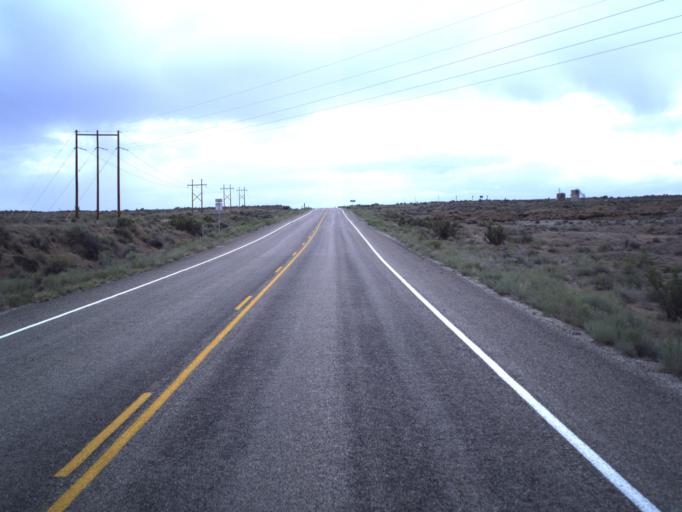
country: US
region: Colorado
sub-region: Rio Blanco County
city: Rangely
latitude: 40.0740
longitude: -109.2064
